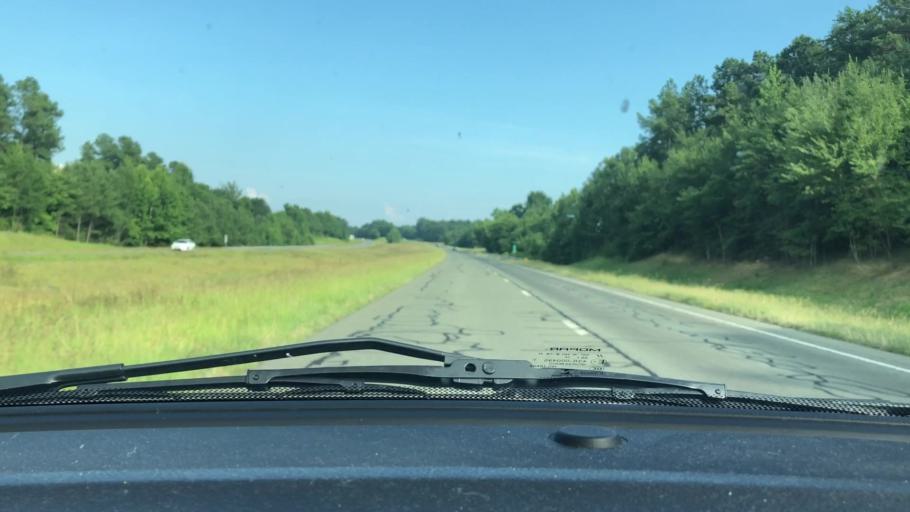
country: US
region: North Carolina
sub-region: Randolph County
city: Liberty
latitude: 35.7954
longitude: -79.5328
